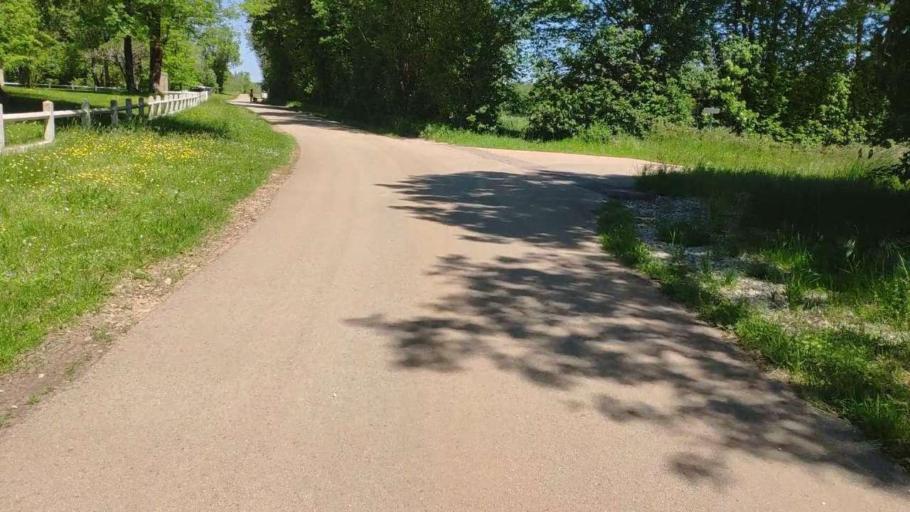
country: FR
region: Franche-Comte
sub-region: Departement du Jura
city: Perrigny
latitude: 46.7199
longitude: 5.6454
